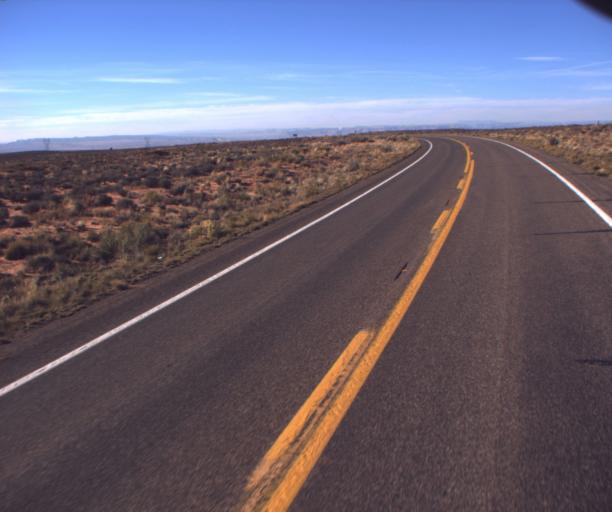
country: US
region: Arizona
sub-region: Coconino County
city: LeChee
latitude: 36.8272
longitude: -111.3098
